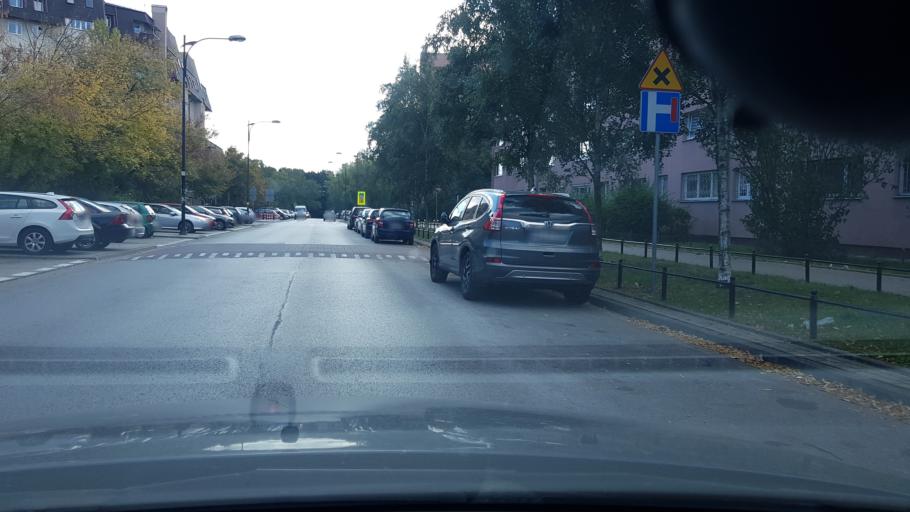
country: PL
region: Masovian Voivodeship
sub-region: Warszawa
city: Bielany
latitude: 52.2913
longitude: 20.9456
